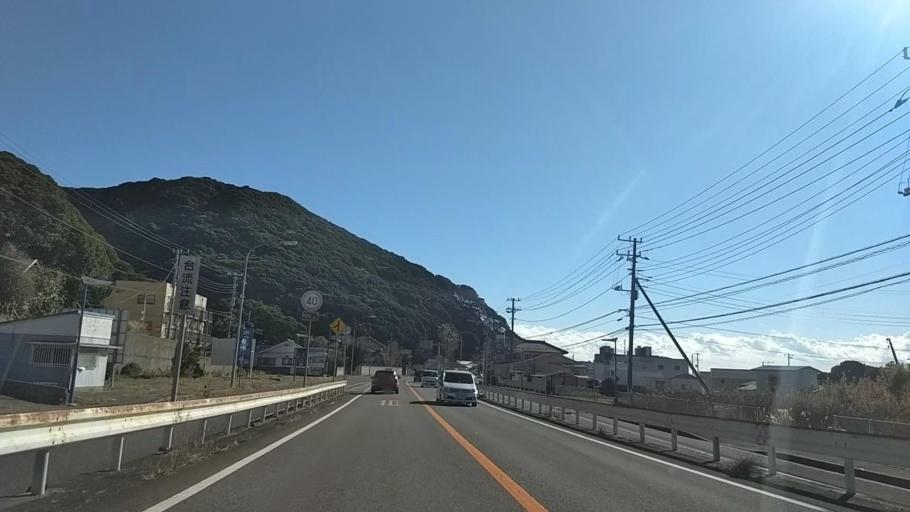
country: JP
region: Chiba
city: Kawaguchi
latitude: 35.1249
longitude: 140.1717
